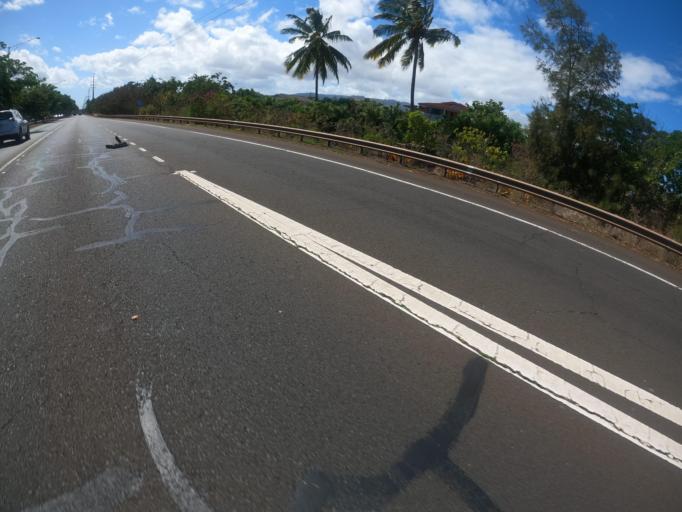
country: US
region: Hawaii
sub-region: Honolulu County
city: Pearl City, Manana
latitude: 21.3921
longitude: -157.9917
